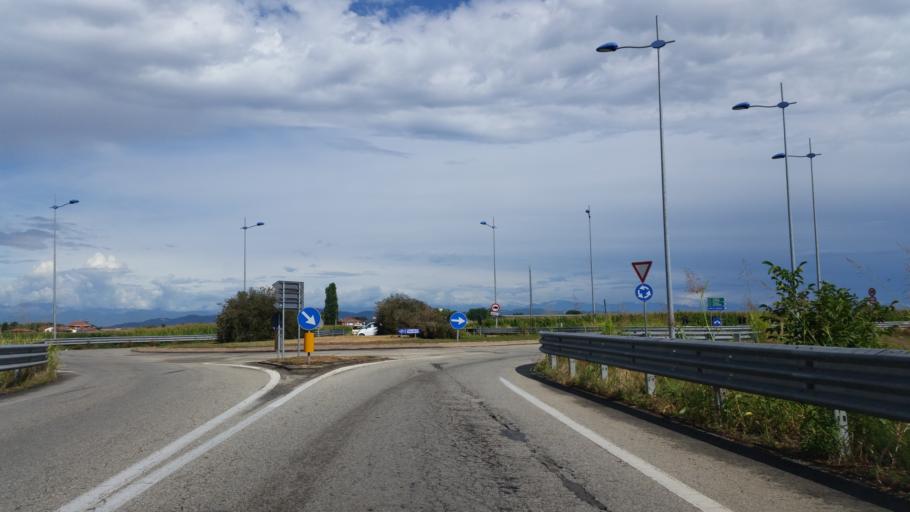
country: IT
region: Piedmont
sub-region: Provincia di Torino
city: Poirino
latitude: 44.9068
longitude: 7.8543
